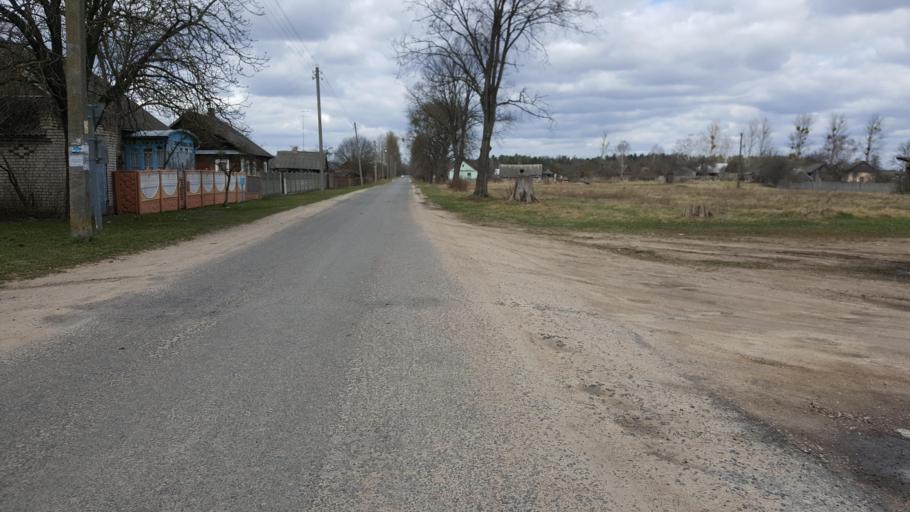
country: PL
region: Podlasie
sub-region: Powiat hajnowski
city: Czeremcha
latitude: 52.4722
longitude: 23.5106
